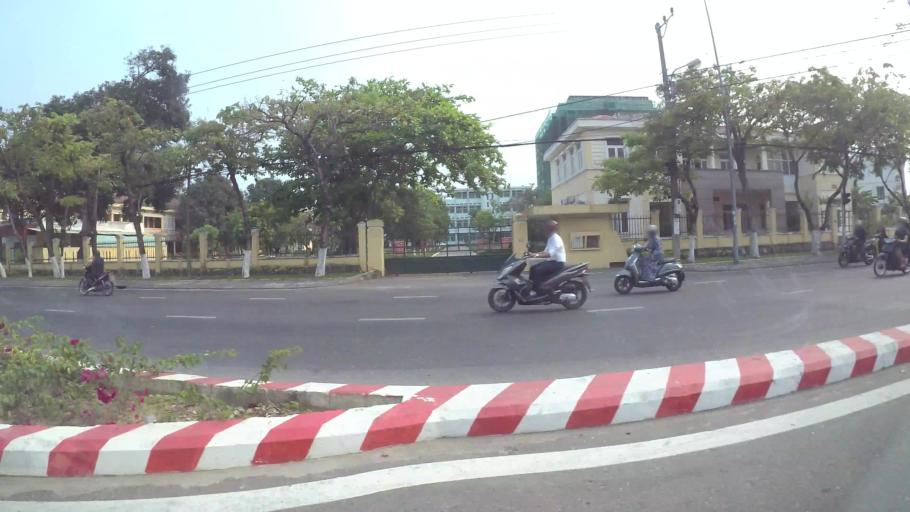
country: VN
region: Da Nang
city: Da Nang
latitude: 16.0483
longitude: 108.2133
